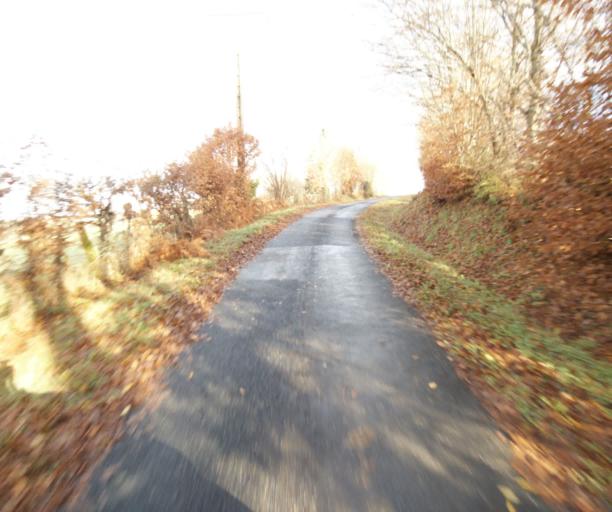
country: FR
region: Limousin
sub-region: Departement de la Correze
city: Saint-Mexant
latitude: 45.2557
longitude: 1.6178
